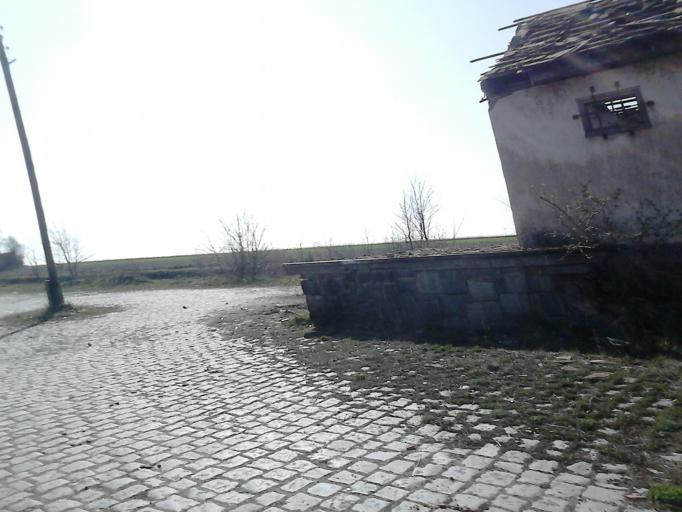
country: PL
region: Lower Silesian Voivodeship
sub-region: Powiat olesnicki
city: Dziadowa Kloda
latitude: 51.1784
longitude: 17.6834
